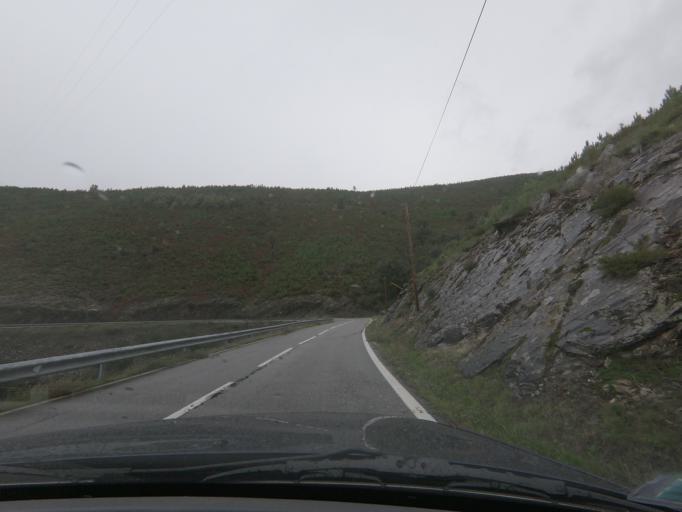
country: PT
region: Vila Real
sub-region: Mondim de Basto
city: Mondim de Basto
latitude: 41.3512
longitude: -7.9054
